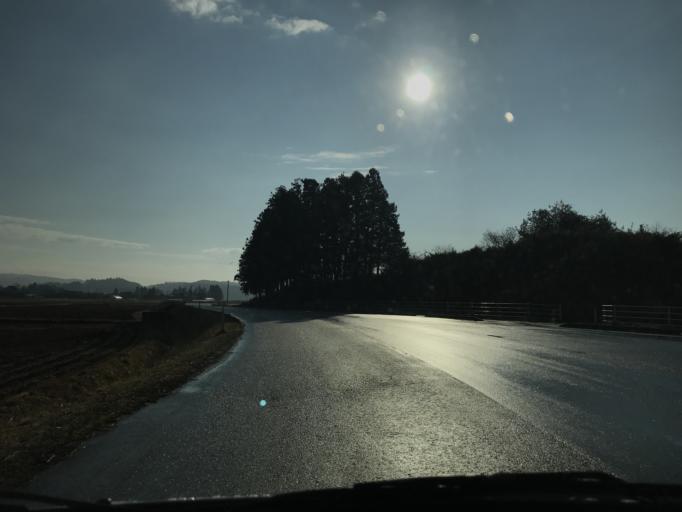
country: JP
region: Iwate
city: Ichinoseki
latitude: 38.7719
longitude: 141.1779
